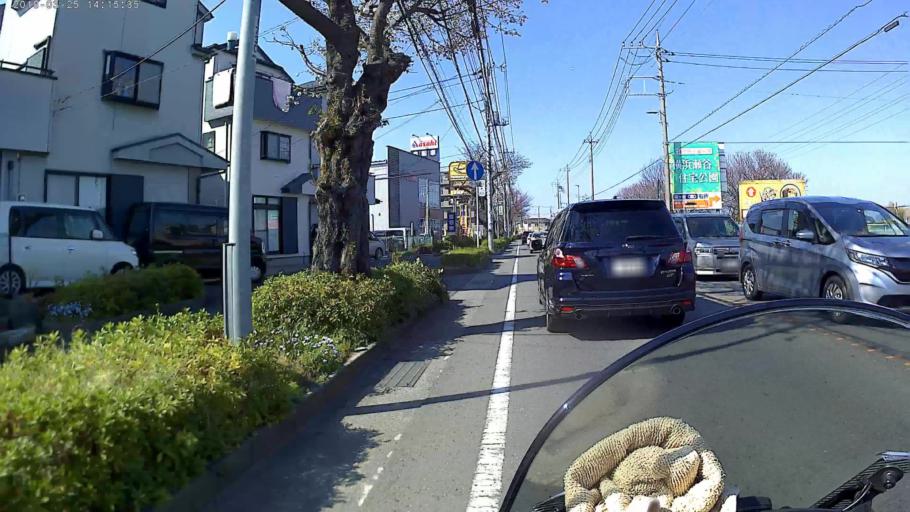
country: JP
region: Kanagawa
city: Minami-rinkan
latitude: 35.4266
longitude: 139.4681
